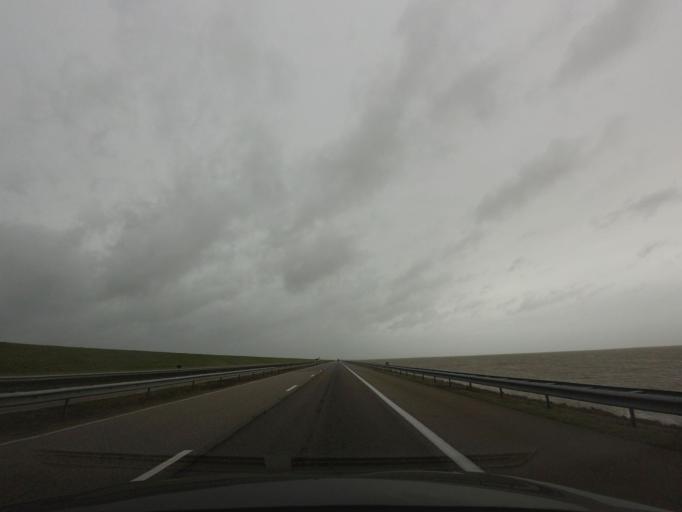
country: NL
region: North Holland
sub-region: Gemeente Hollands Kroon
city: Den Oever
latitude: 52.9857
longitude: 5.1405
